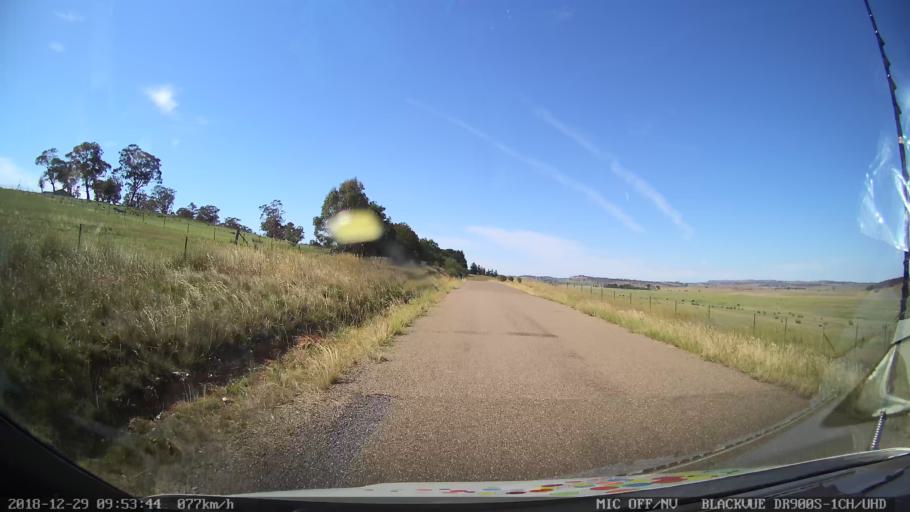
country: AU
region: New South Wales
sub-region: Goulburn Mulwaree
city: Goulburn
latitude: -34.7551
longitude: 149.4687
